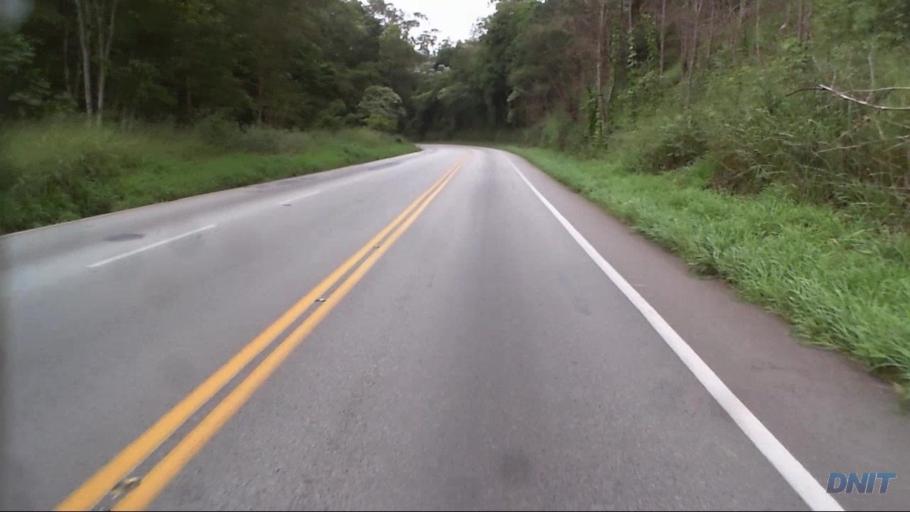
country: BR
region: Minas Gerais
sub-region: Joao Monlevade
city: Joao Monlevade
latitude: -19.8461
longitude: -43.1081
